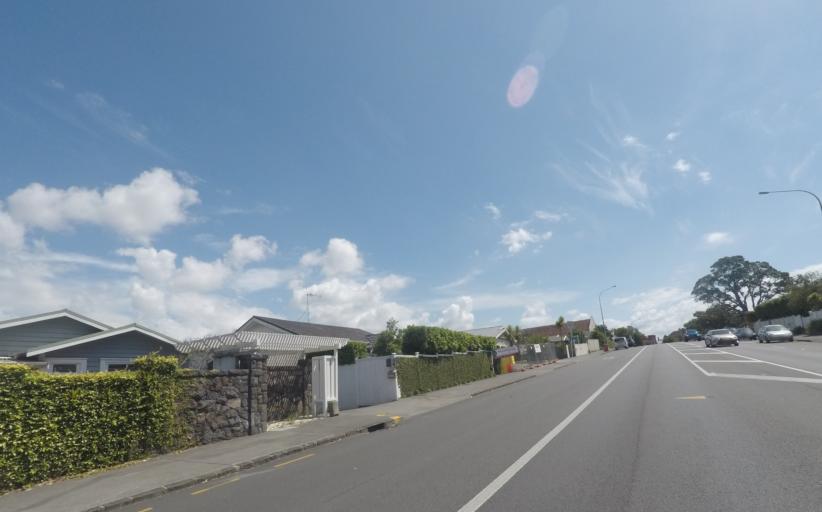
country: NZ
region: Auckland
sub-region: Auckland
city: Tamaki
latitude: -36.8799
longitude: 174.8170
